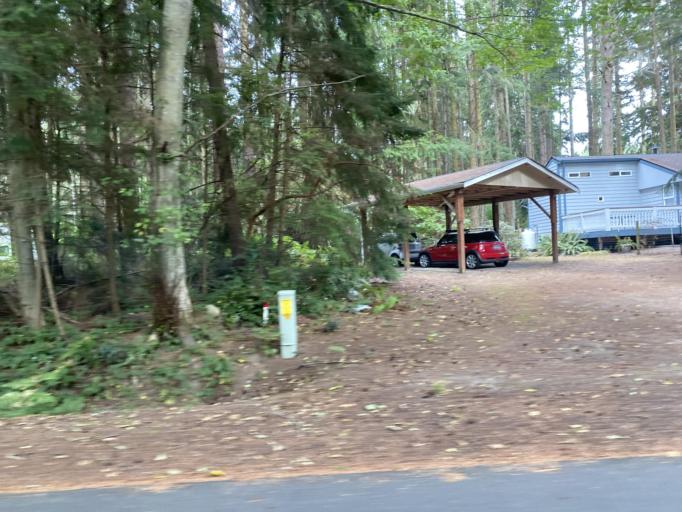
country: US
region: Washington
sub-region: Island County
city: Freeland
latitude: 48.0670
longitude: -122.5115
